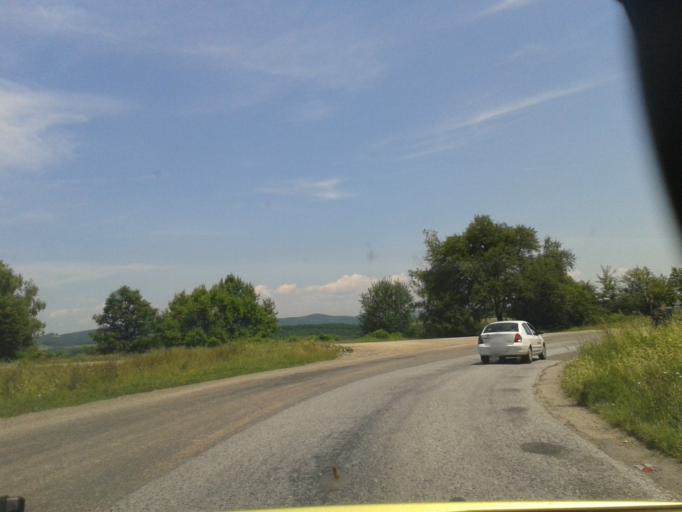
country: RO
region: Timis
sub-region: Comuna Pietroasa
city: Pietroasa
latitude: 45.8856
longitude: 22.4236
